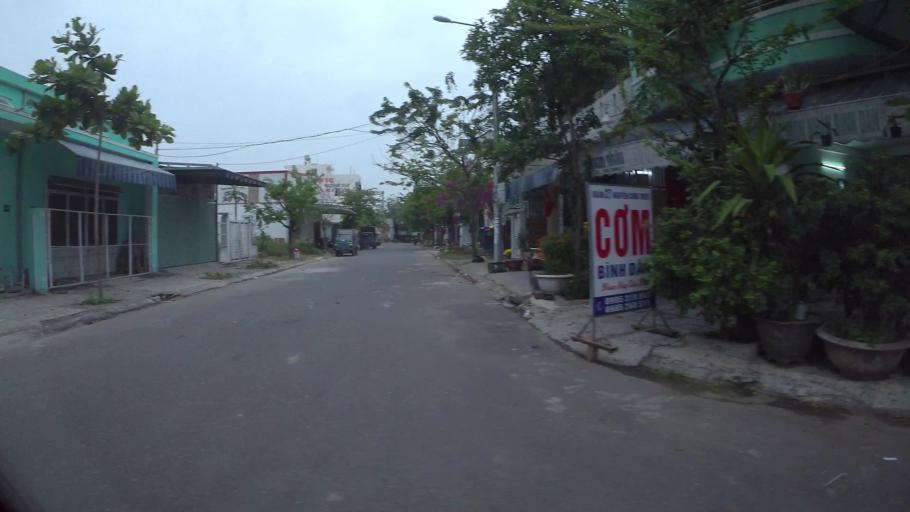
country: VN
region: Da Nang
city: Thanh Khe
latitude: 16.0459
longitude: 108.1784
